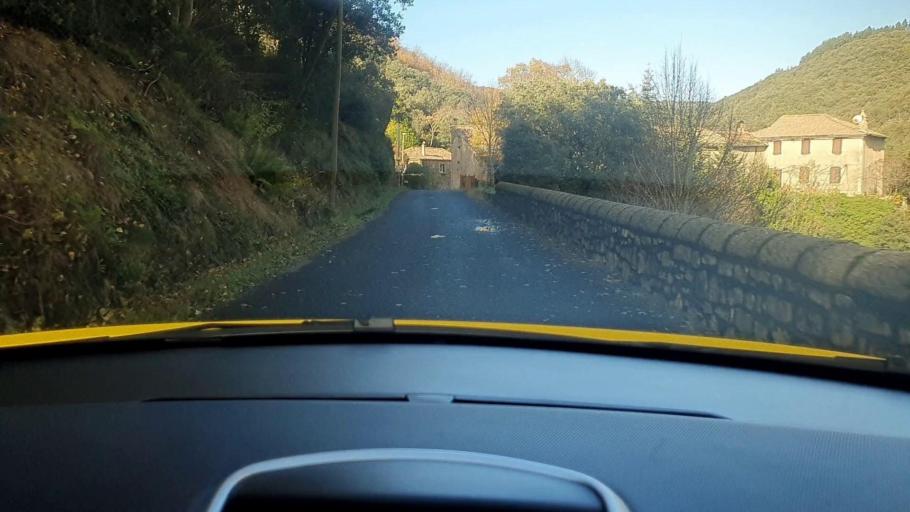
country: FR
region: Languedoc-Roussillon
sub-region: Departement du Gard
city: Valleraugue
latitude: 44.1038
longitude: 3.7322
